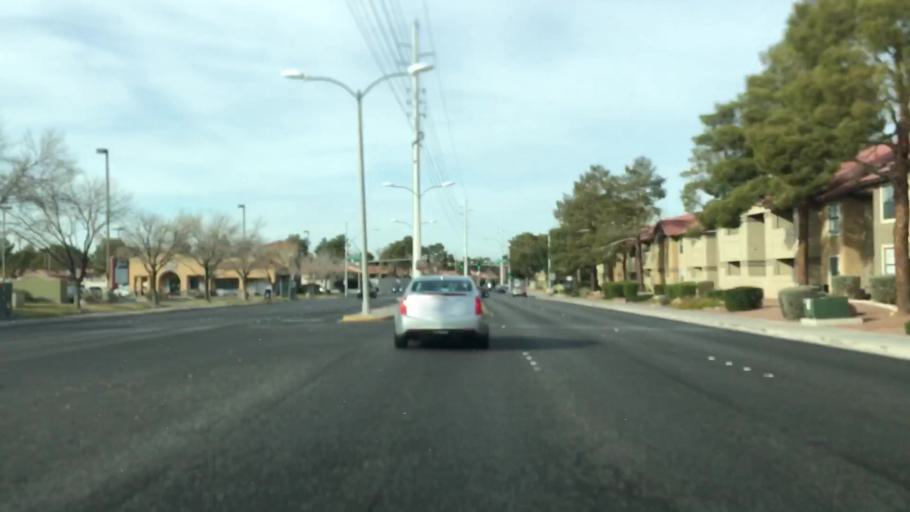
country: US
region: Nevada
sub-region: Clark County
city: Whitney
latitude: 36.0551
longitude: -115.0835
